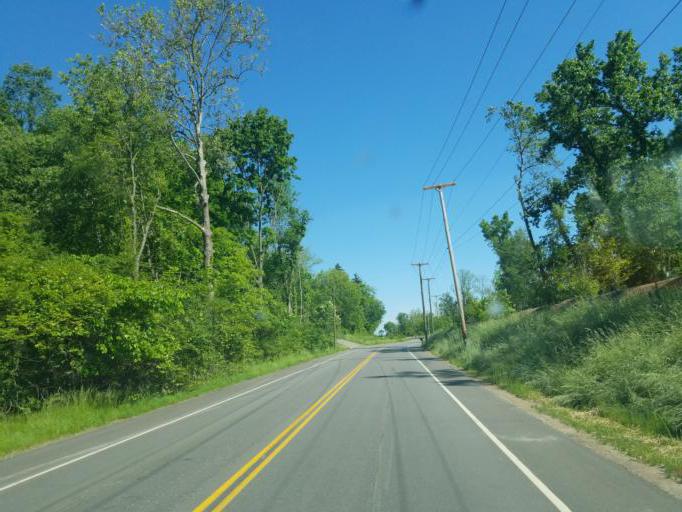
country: US
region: Ohio
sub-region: Summit County
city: Fairlawn
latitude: 41.1432
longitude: -81.5653
